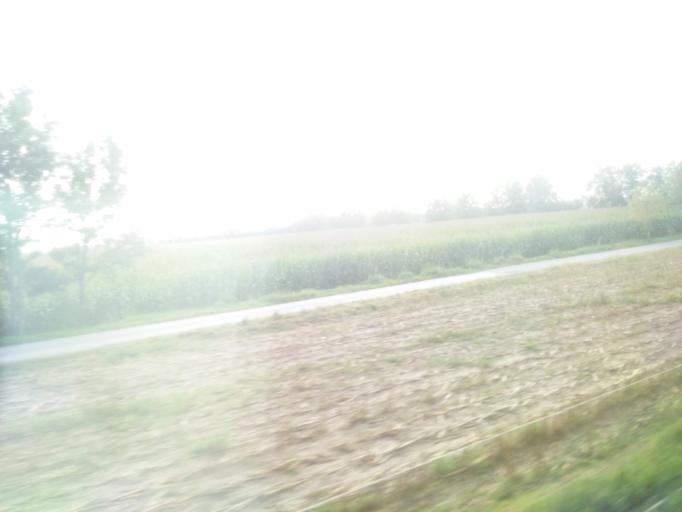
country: IT
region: Lombardy
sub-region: Provincia di Bergamo
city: Cortenuova
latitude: 45.5261
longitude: 9.7941
